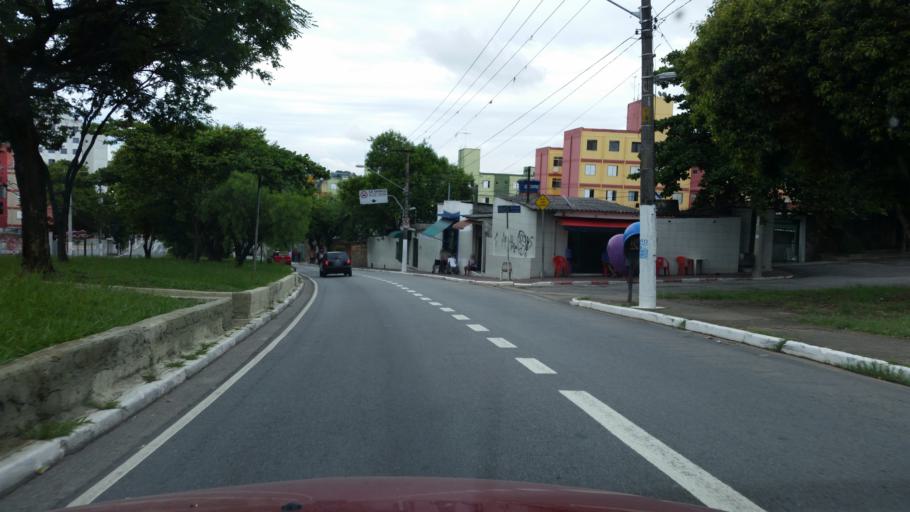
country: BR
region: Sao Paulo
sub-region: Ferraz De Vasconcelos
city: Ferraz de Vasconcelos
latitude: -23.5507
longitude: -46.4387
